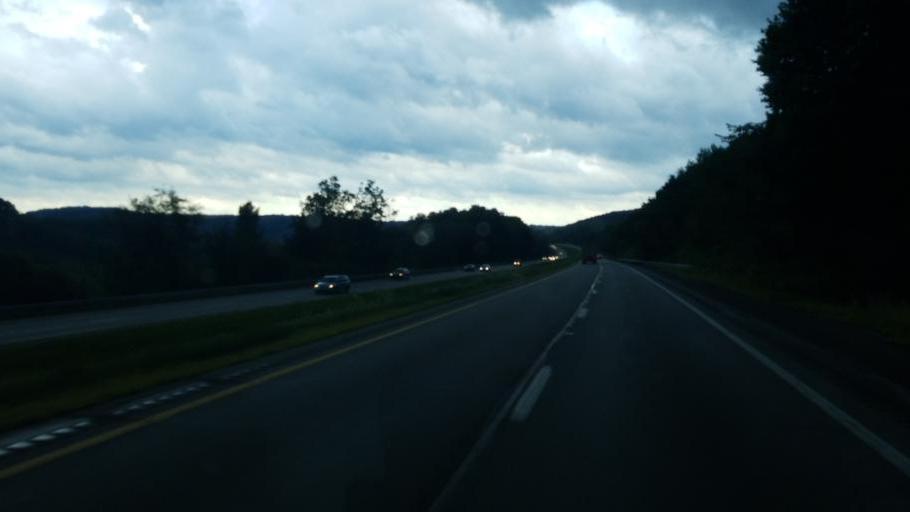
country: US
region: Pennsylvania
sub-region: Butler County
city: Prospect
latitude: 40.8660
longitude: -80.1111
